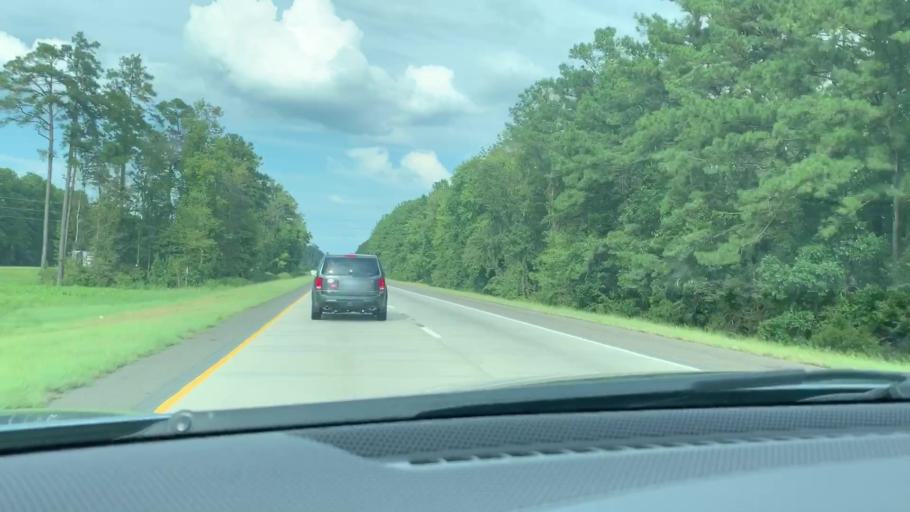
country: US
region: South Carolina
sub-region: Colleton County
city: Walterboro
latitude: 32.8482
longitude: -80.7350
